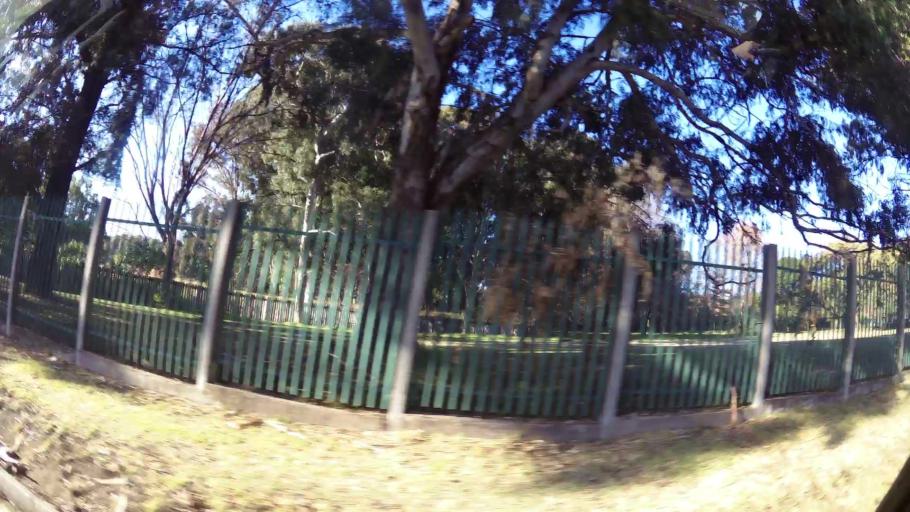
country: ZA
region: Gauteng
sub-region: City of Johannesburg Metropolitan Municipality
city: Johannesburg
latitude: -26.1902
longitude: 28.0966
